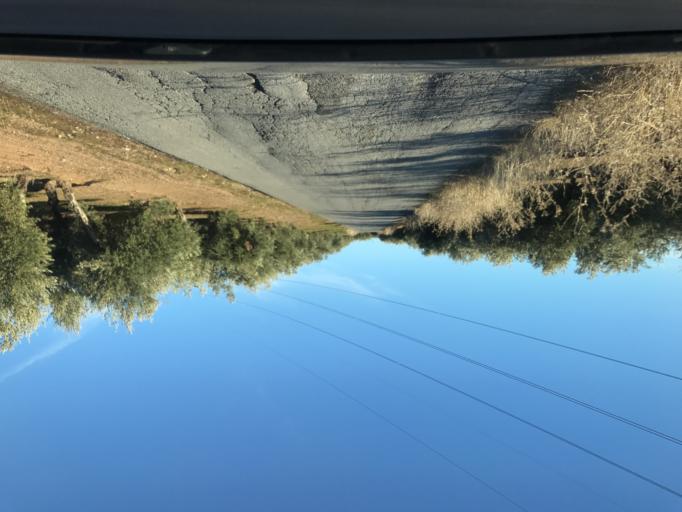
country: ES
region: Andalusia
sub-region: Provincia de Granada
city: Calicasas
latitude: 37.2640
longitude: -3.6111
